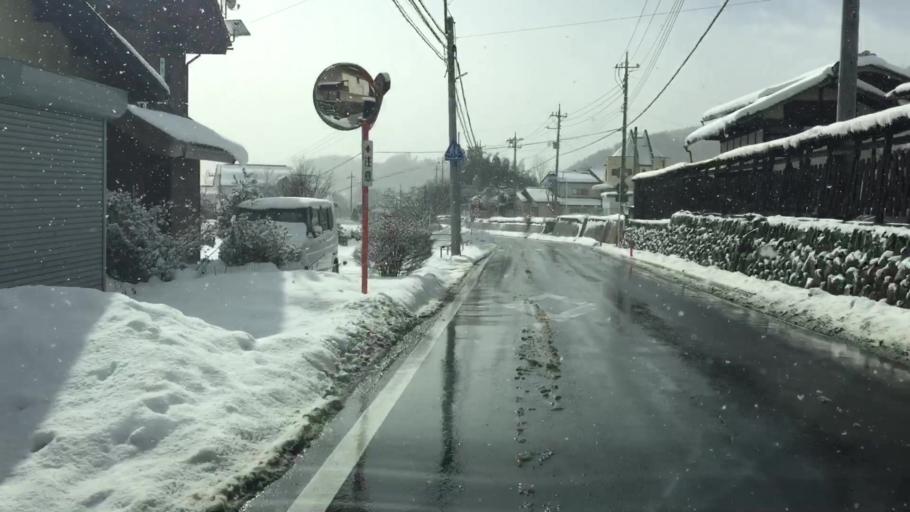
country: JP
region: Gunma
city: Numata
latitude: 36.6930
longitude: 139.0641
